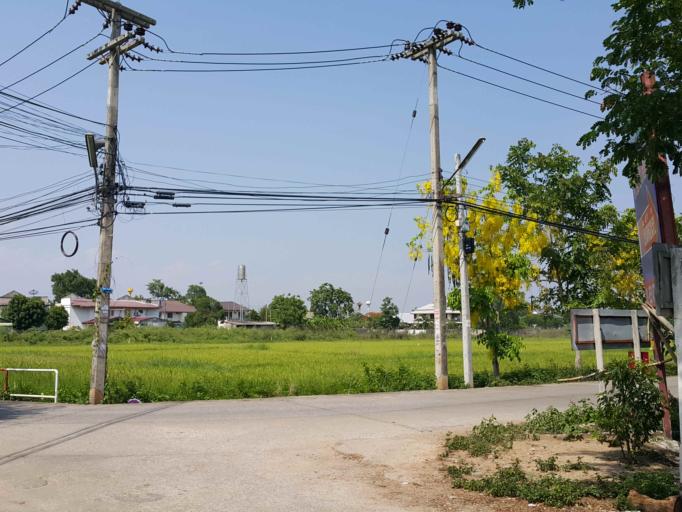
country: TH
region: Chiang Mai
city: Chiang Mai
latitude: 18.7326
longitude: 98.9650
